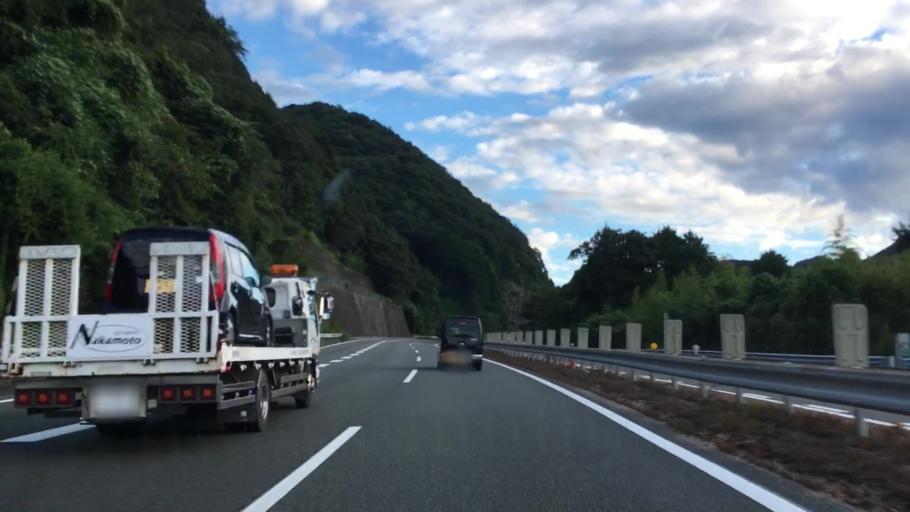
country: JP
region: Yamaguchi
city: Onoda
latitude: 34.1549
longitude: 131.2358
